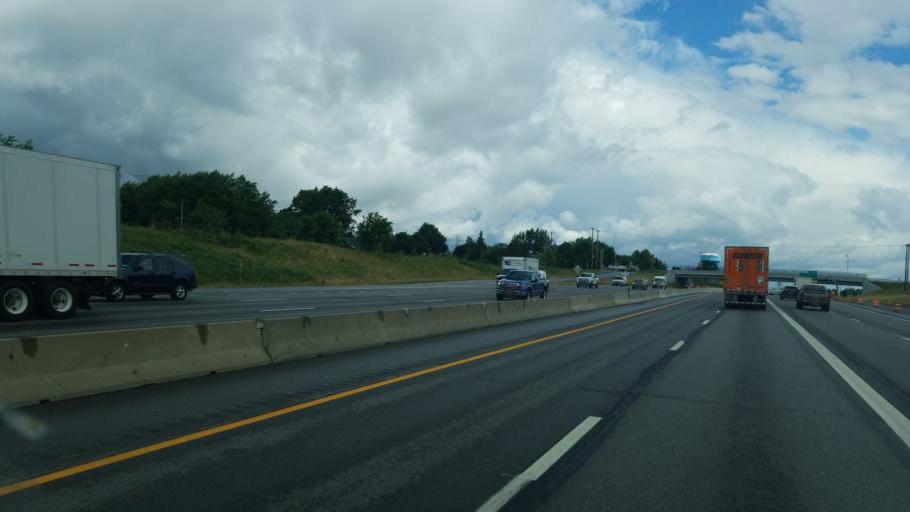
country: US
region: New York
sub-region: Erie County
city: Williamsville
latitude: 42.9425
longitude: -78.7663
